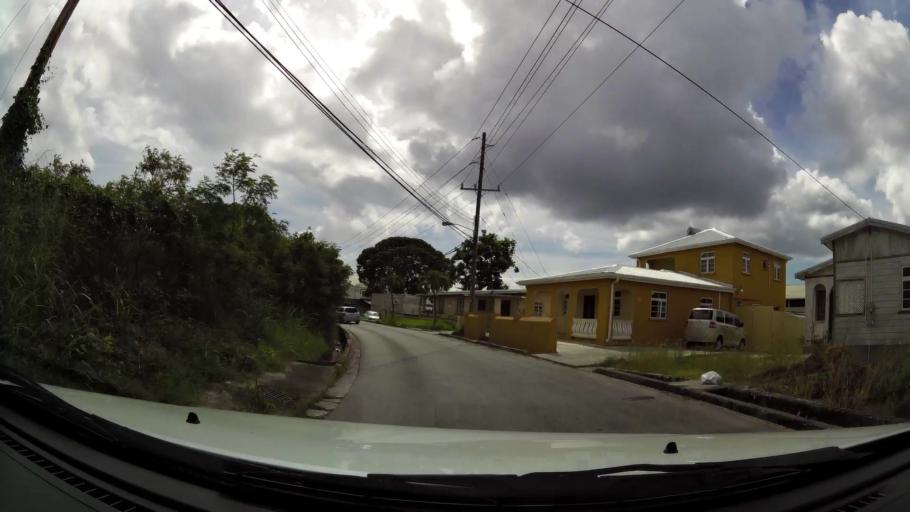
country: BB
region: Saint Michael
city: Bridgetown
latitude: 13.1127
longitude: -59.6250
